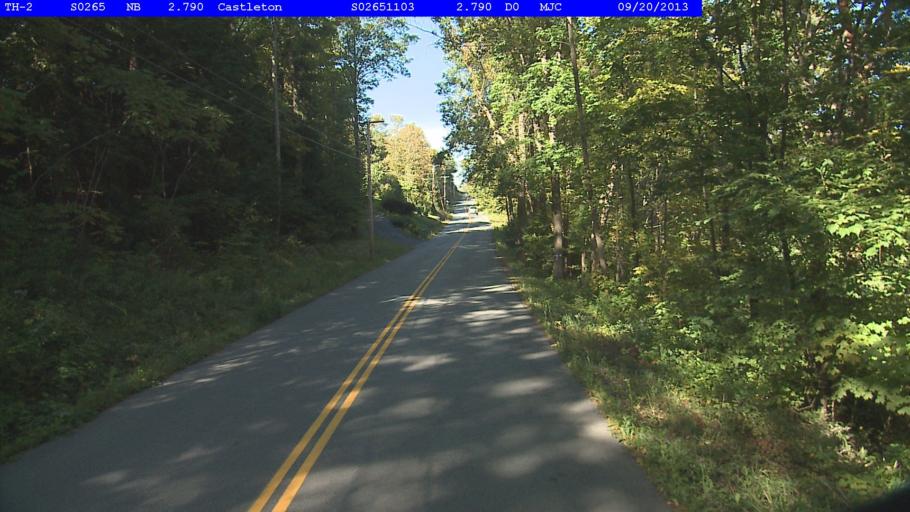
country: US
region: Vermont
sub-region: Rutland County
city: Fair Haven
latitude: 43.6411
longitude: -73.2341
